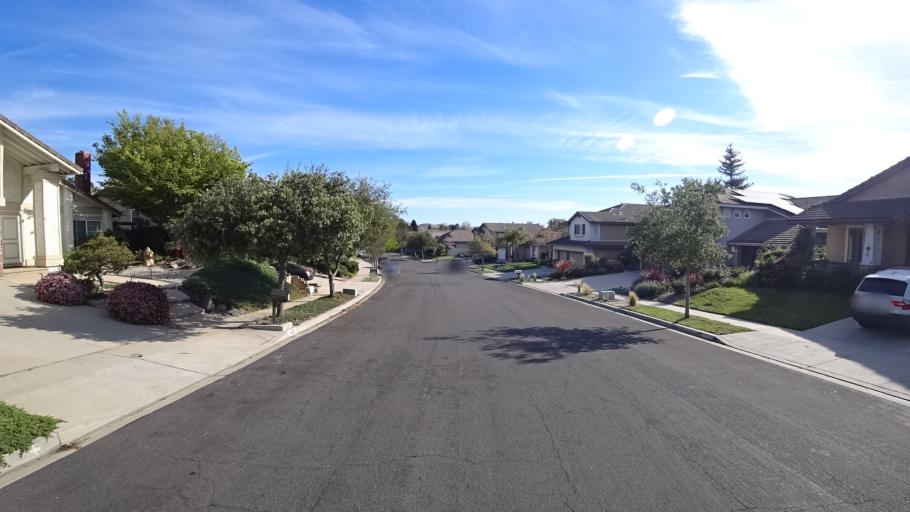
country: US
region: California
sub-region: Ventura County
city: Casa Conejo
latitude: 34.1712
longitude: -118.9584
